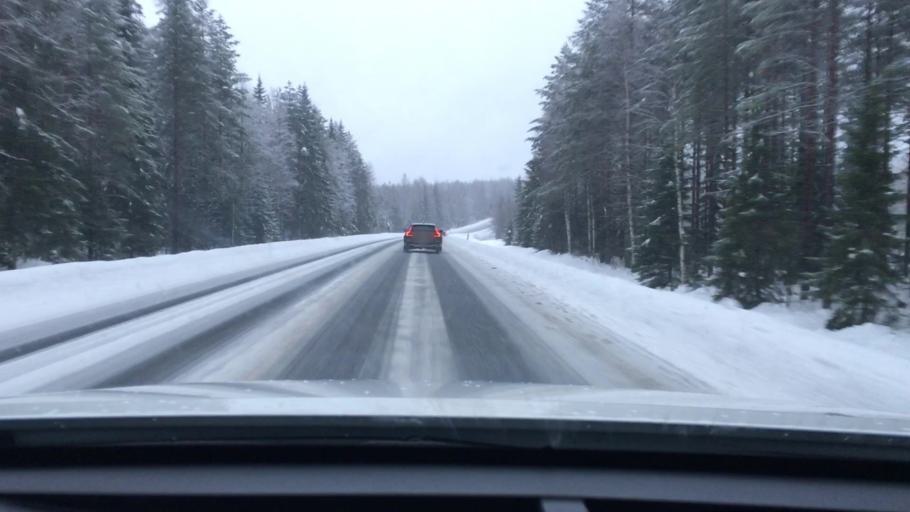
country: FI
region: Northern Savo
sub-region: Ylae-Savo
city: Sonkajaervi
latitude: 63.7714
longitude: 27.4149
